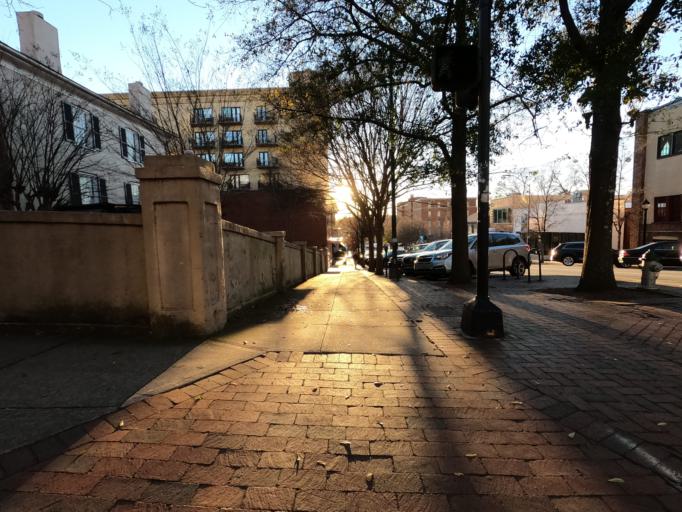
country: US
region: Georgia
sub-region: Clarke County
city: Athens
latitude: 33.9578
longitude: -83.3786
